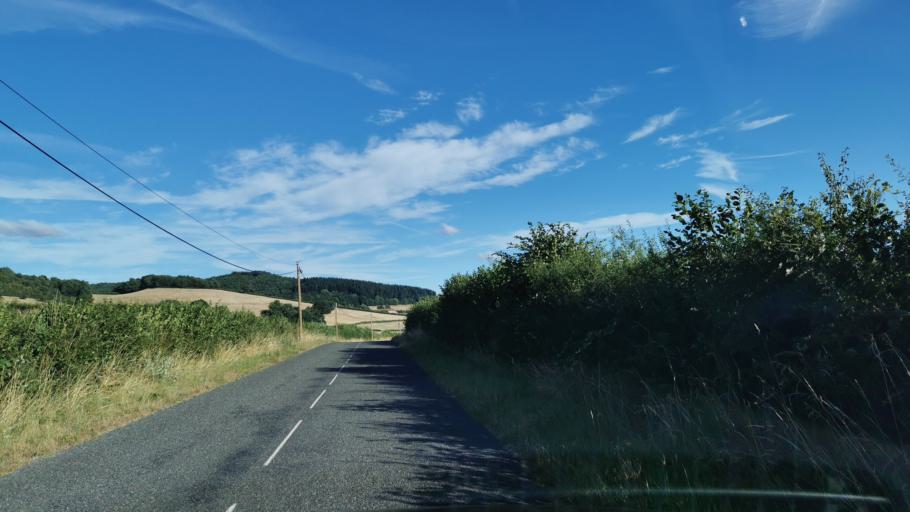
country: FR
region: Bourgogne
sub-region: Departement de Saone-et-Loire
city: Marmagne
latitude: 46.8200
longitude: 4.3253
